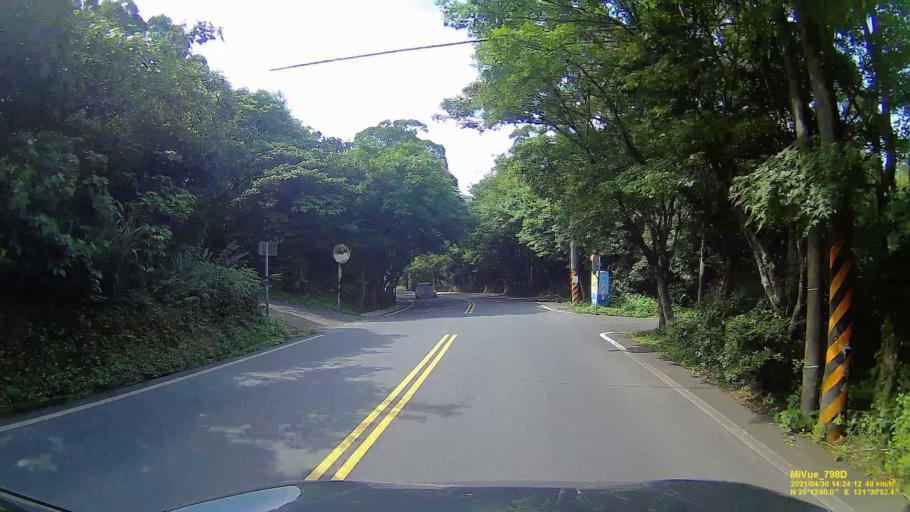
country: TW
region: Taipei
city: Taipei
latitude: 25.2281
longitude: 121.5144
